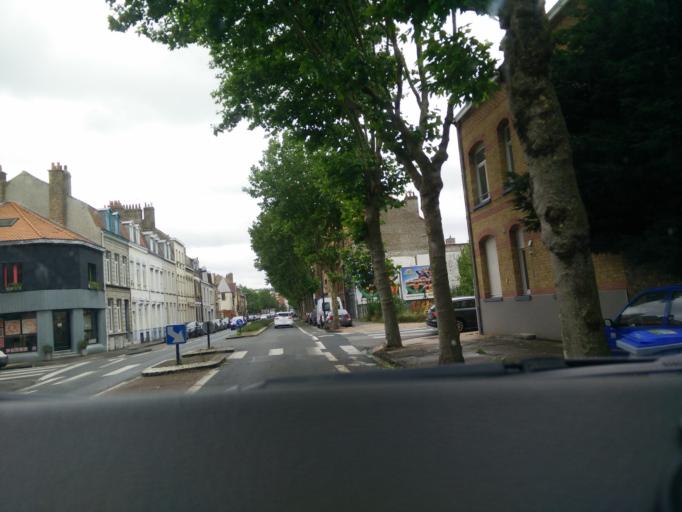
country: FR
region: Nord-Pas-de-Calais
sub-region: Departement du Nord
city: Coudekerque-Branche
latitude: 51.0430
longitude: 2.3964
